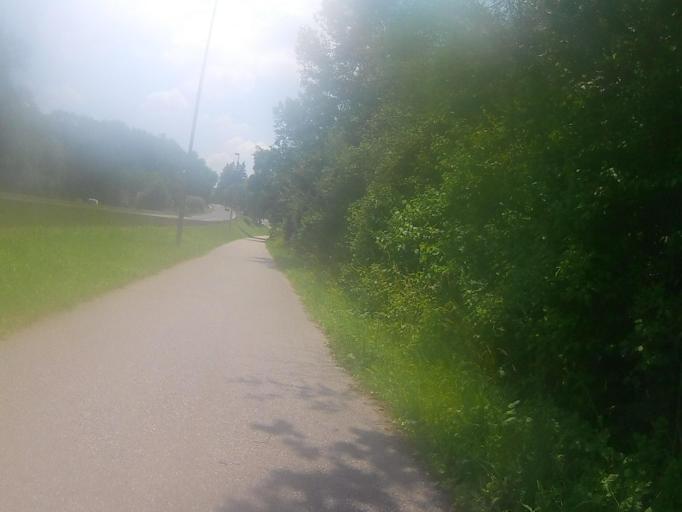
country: SI
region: Maribor
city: Kamnica
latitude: 46.5688
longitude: 15.6195
